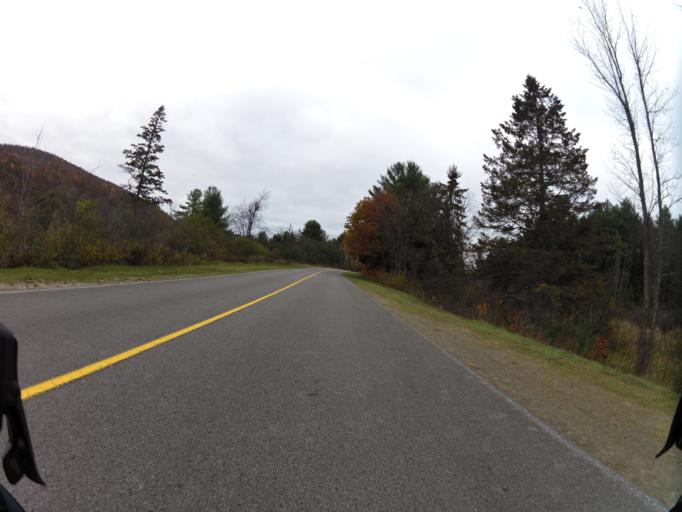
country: CA
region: Quebec
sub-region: Outaouais
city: Gatineau
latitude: 45.5070
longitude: -75.8228
